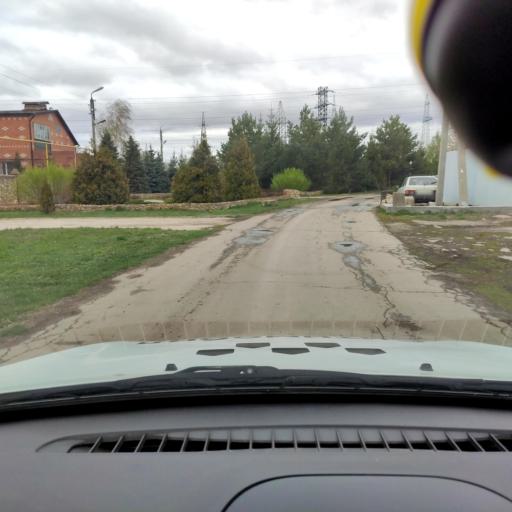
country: RU
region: Samara
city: Tol'yatti
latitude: 53.5849
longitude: 49.3309
